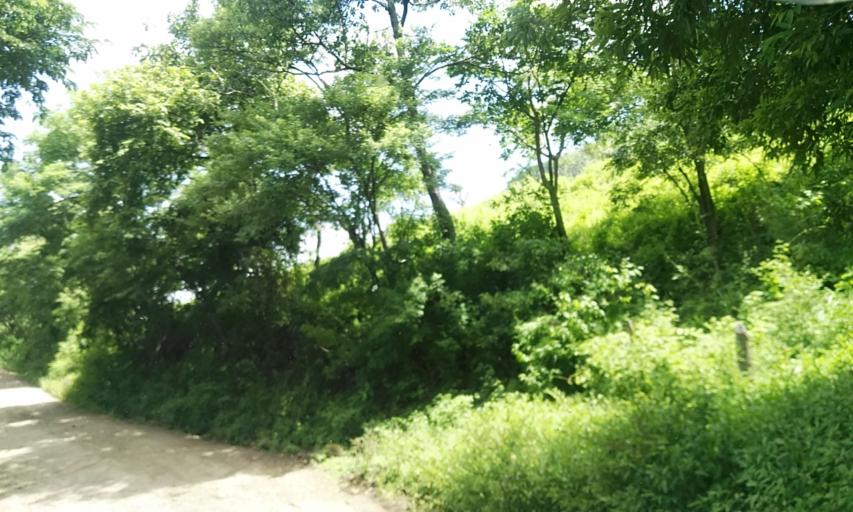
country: NI
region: Matagalpa
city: Terrabona
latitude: 12.7283
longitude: -85.9298
